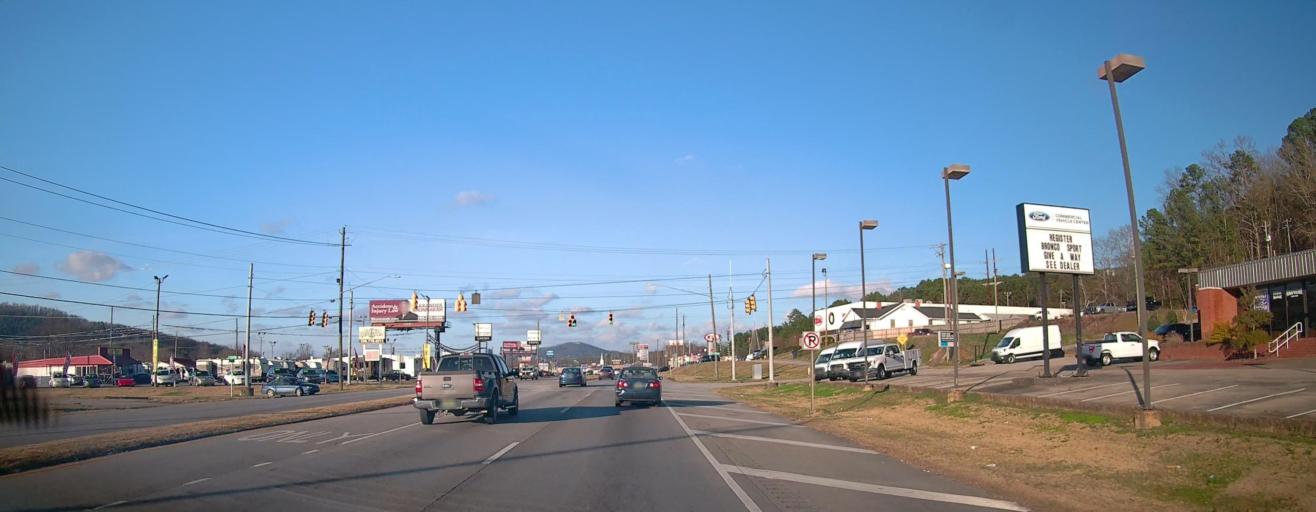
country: US
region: Alabama
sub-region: Calhoun County
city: Oxford
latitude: 33.6287
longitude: -85.8265
